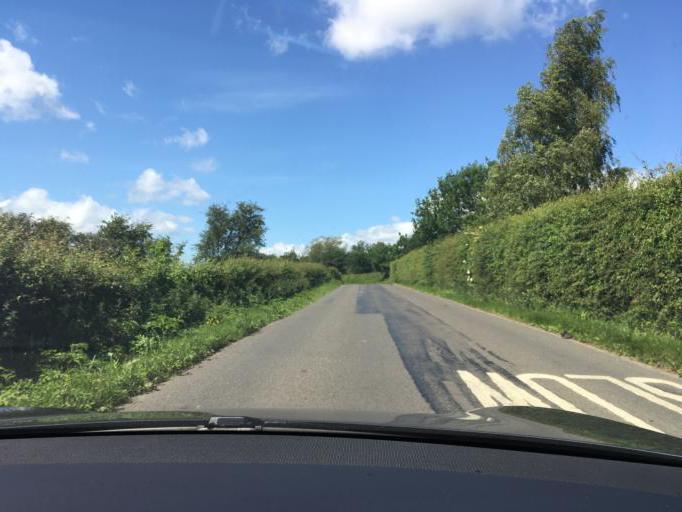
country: GB
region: England
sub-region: Cheshire East
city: Mobberley
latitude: 53.2896
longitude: -2.3267
